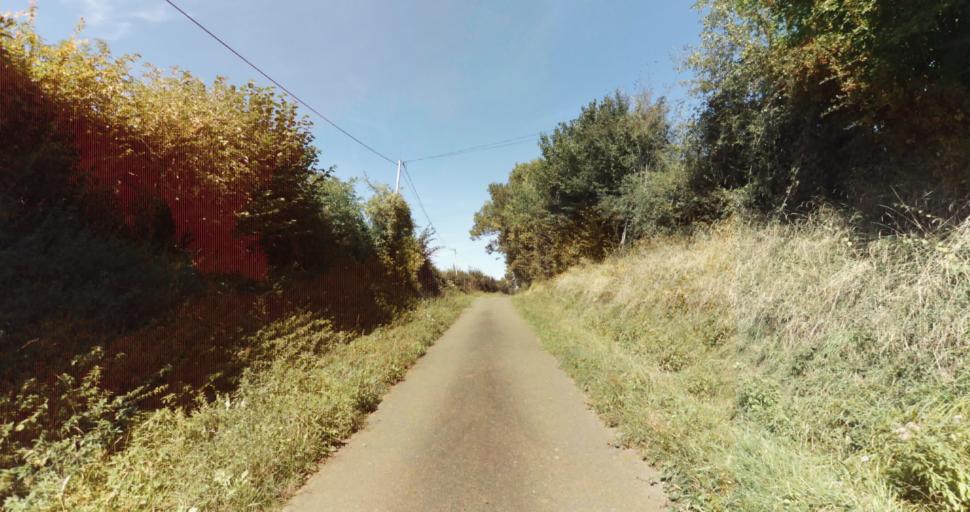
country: FR
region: Lower Normandy
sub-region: Departement de l'Orne
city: Gace
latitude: 48.7610
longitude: 0.2685
